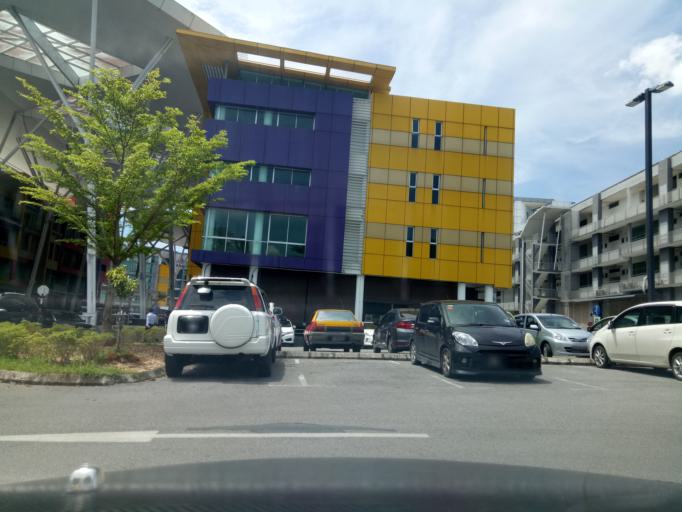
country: MY
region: Sarawak
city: Kuching
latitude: 1.5513
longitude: 110.3712
